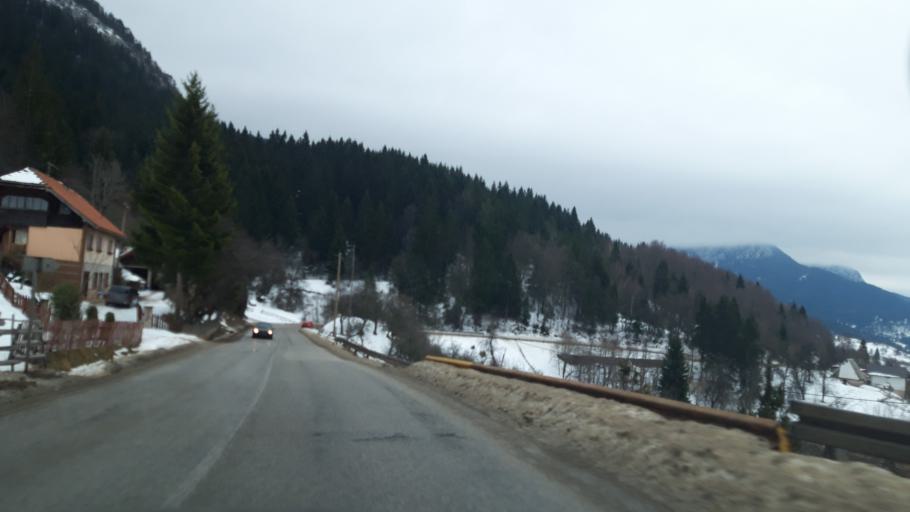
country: BA
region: Republika Srpska
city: Pale
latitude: 43.9040
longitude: 18.6368
